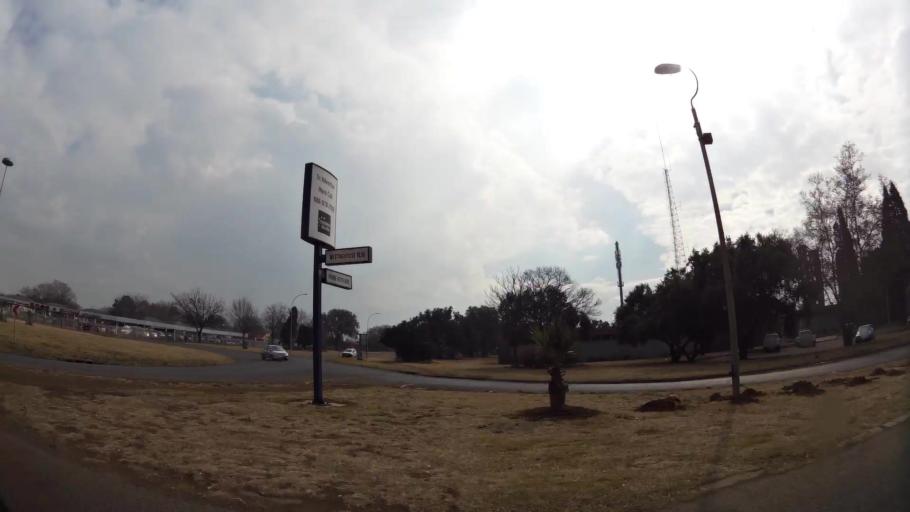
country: ZA
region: Gauteng
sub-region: Sedibeng District Municipality
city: Vanderbijlpark
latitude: -26.6838
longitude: 27.8351
